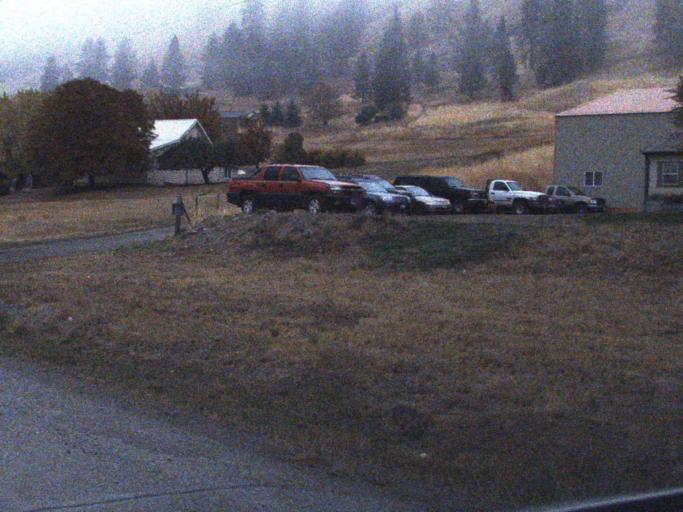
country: US
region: Washington
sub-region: Stevens County
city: Kettle Falls
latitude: 48.6111
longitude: -118.0385
